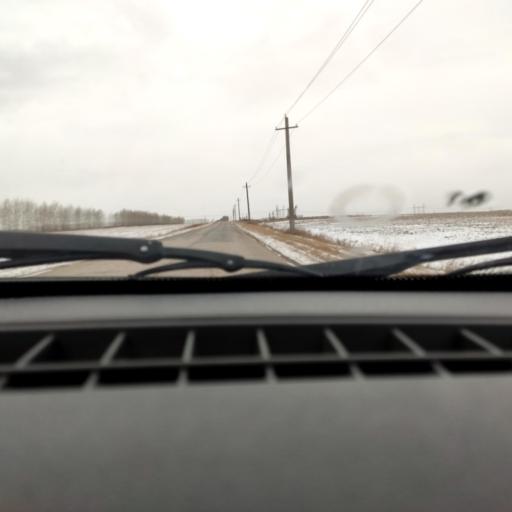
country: RU
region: Bashkortostan
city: Tolbazy
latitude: 54.2486
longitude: 55.8988
